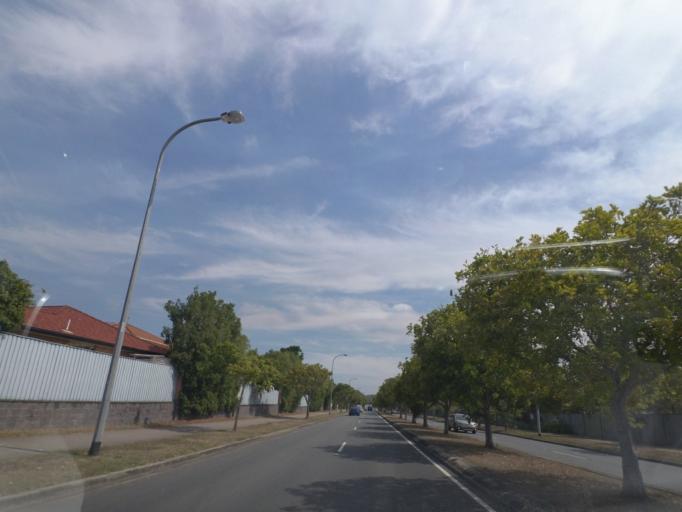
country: AU
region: Queensland
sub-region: Brisbane
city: Sunnybank Hills
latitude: -27.6282
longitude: 153.0590
